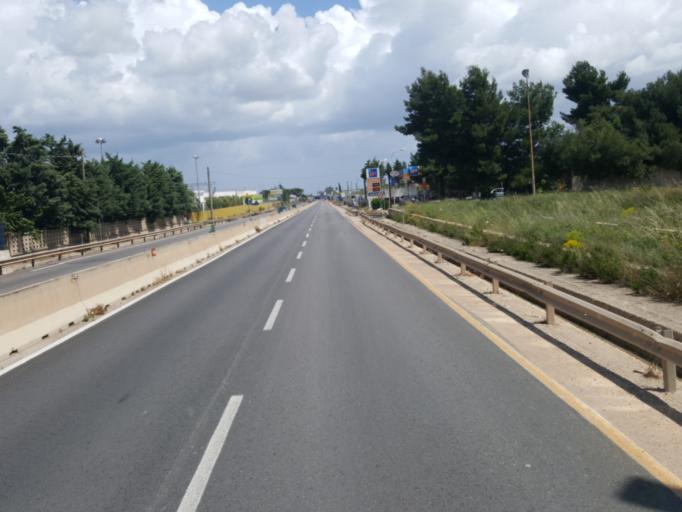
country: IT
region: Apulia
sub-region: Provincia di Bari
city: Bitetto
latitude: 41.0771
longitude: 16.7582
